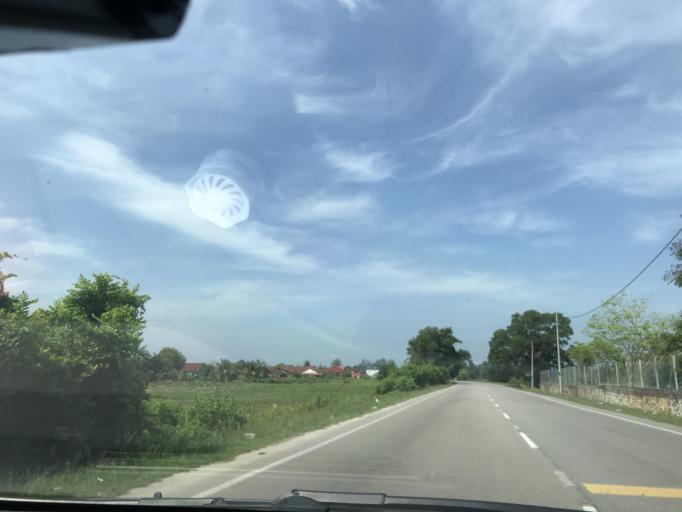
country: MY
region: Kelantan
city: Tumpat
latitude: 6.2008
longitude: 102.1561
